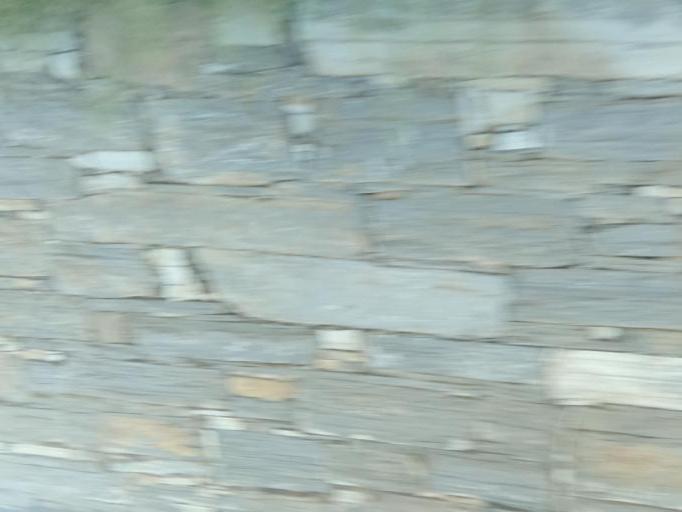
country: PT
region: Vila Real
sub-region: Santa Marta de Penaguiao
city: Santa Marta de Penaguiao
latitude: 41.1981
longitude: -7.7665
